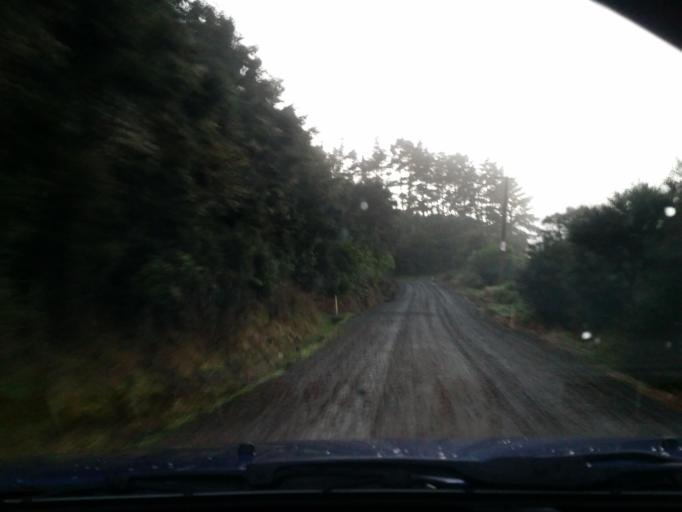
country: NZ
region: Northland
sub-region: Whangarei
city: Maungatapere
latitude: -35.8055
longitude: 174.0446
